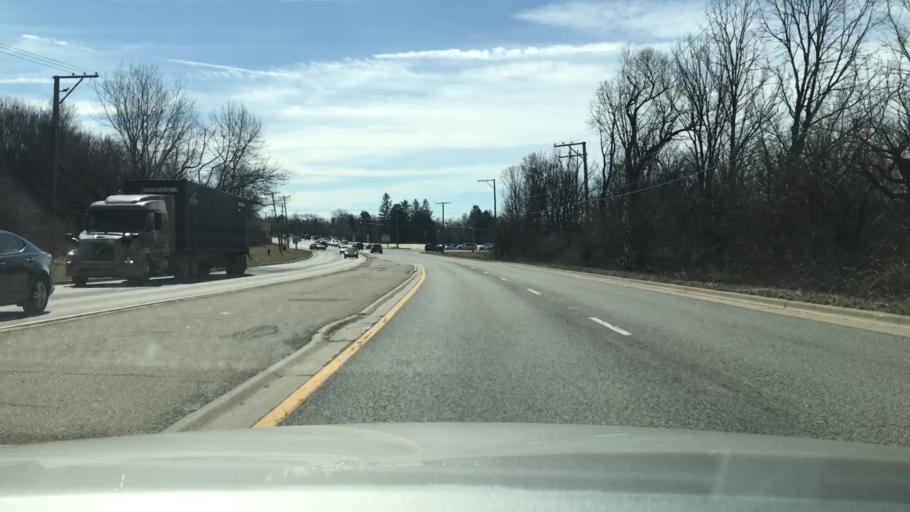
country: US
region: Illinois
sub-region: DuPage County
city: Woodridge
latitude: 41.7517
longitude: -88.0646
